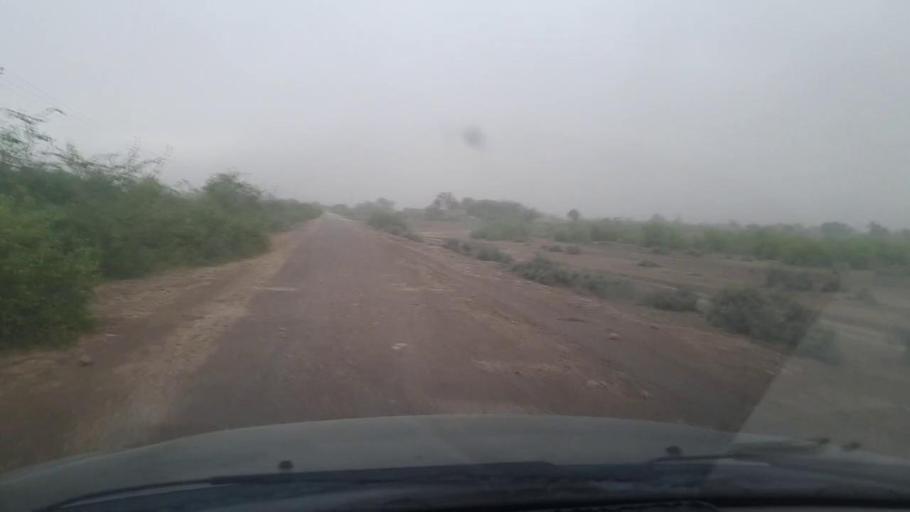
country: PK
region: Sindh
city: Digri
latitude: 25.0013
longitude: 69.1030
